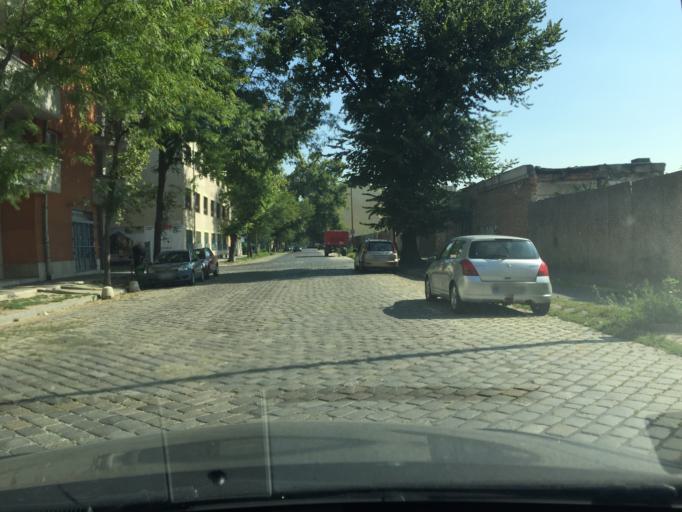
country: HU
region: Budapest
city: Budapest VI. keruelet
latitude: 47.5178
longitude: 19.0681
